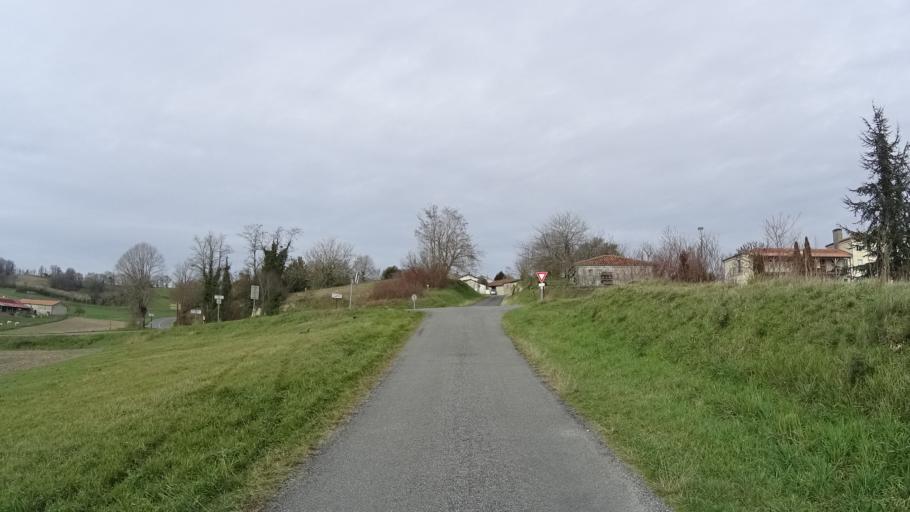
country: FR
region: Aquitaine
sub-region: Departement de la Dordogne
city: Saint-Aulaye
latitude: 45.2662
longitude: 0.1692
